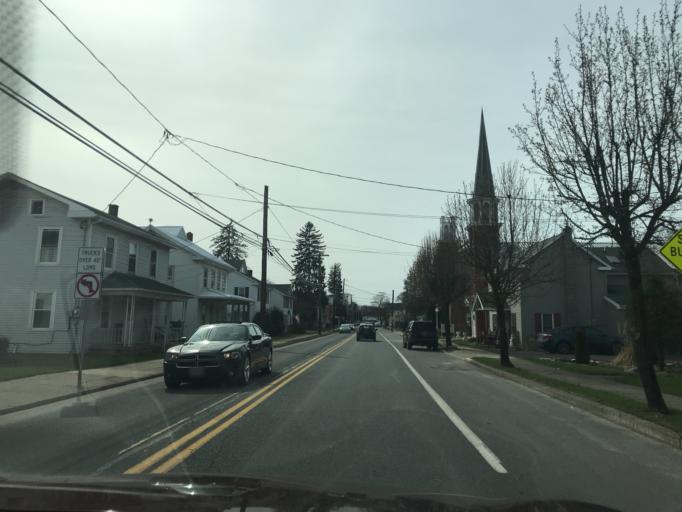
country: US
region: Pennsylvania
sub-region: Union County
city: Lewisburg
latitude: 40.9659
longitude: -76.8543
